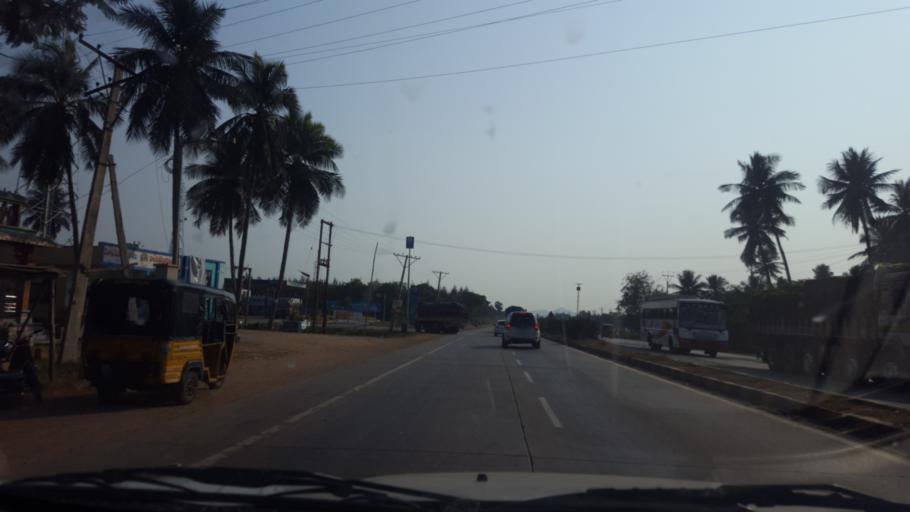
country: IN
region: Andhra Pradesh
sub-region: Vishakhapatnam
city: Elamanchili
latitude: 17.5952
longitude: 82.8722
